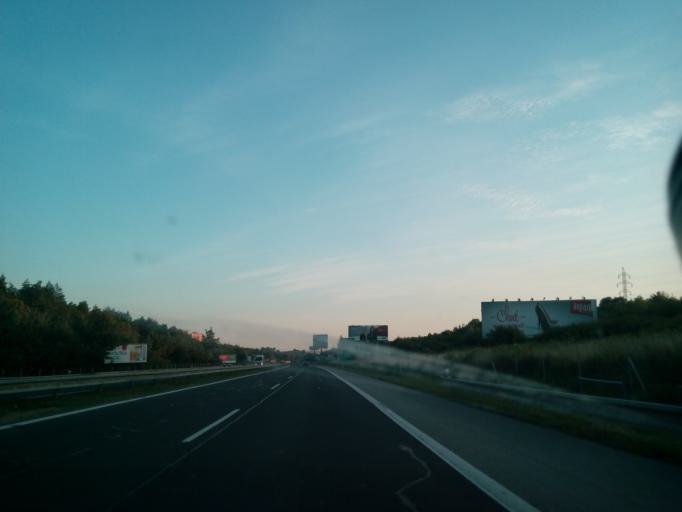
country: SK
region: Kosicky
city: Kosice
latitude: 48.7525
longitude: 21.2775
